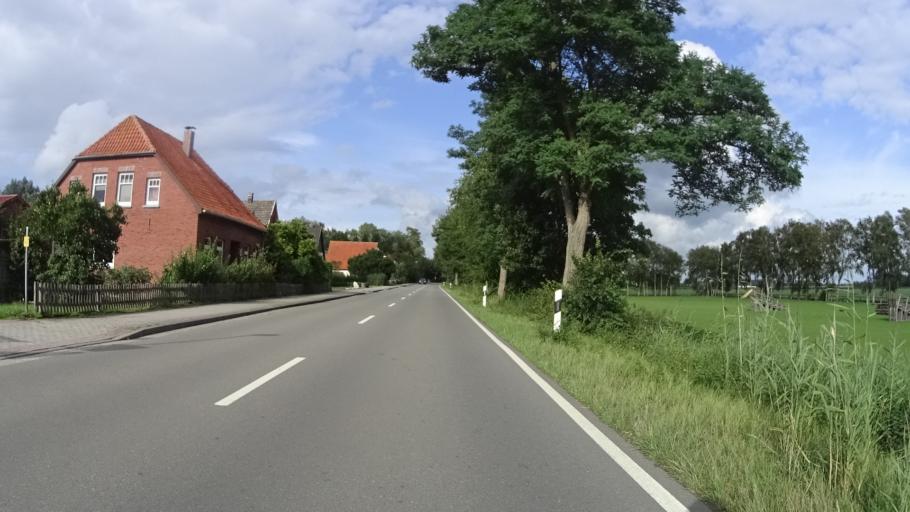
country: DE
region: Lower Saxony
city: Varel
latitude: 53.3864
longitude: 8.2406
